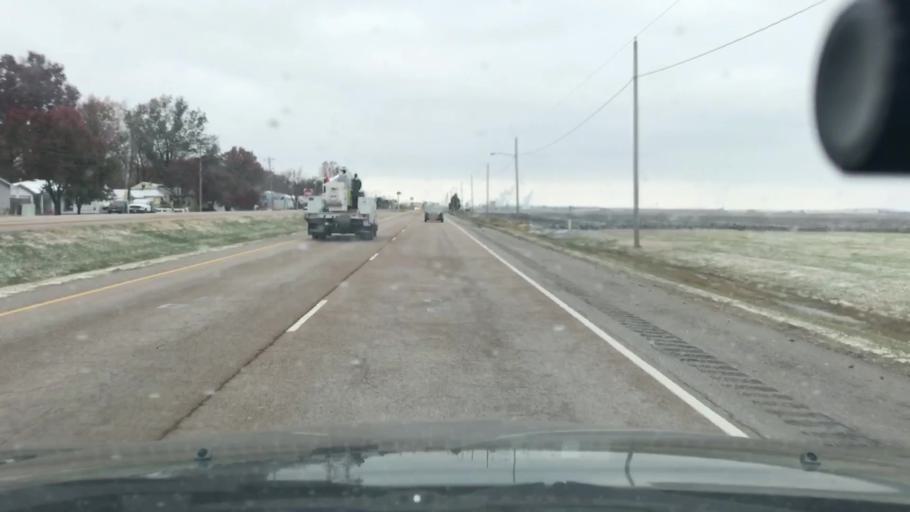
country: US
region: Illinois
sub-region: Madison County
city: Pontoon Beach
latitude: 38.7347
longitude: -90.0709
